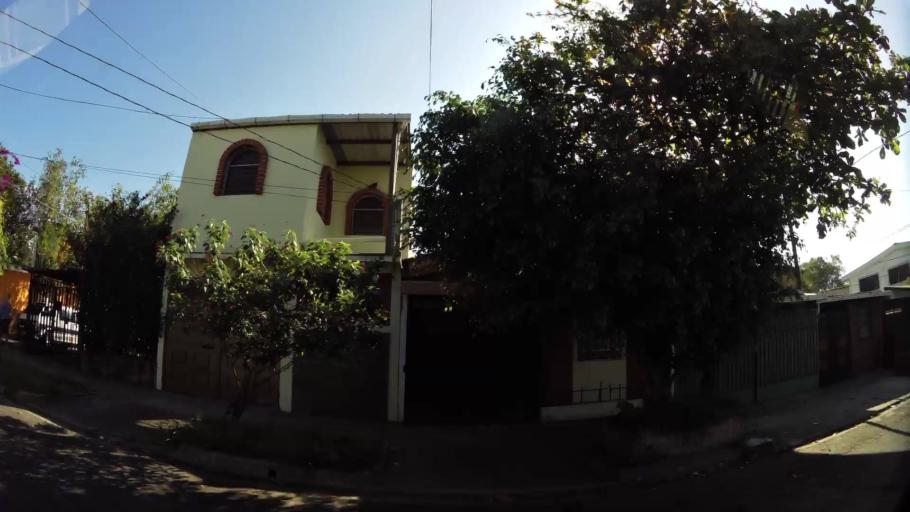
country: SV
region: La Libertad
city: Santa Tecla
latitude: 13.6809
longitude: -89.2923
